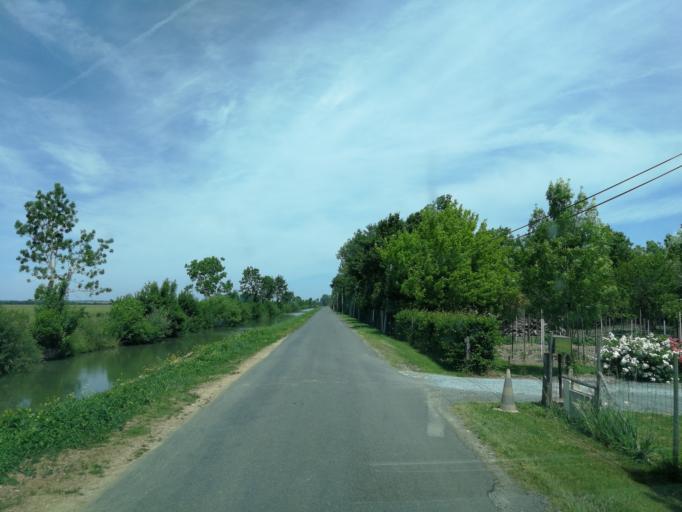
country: FR
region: Pays de la Loire
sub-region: Departement de la Vendee
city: Le Langon
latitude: 46.4078
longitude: -0.9242
